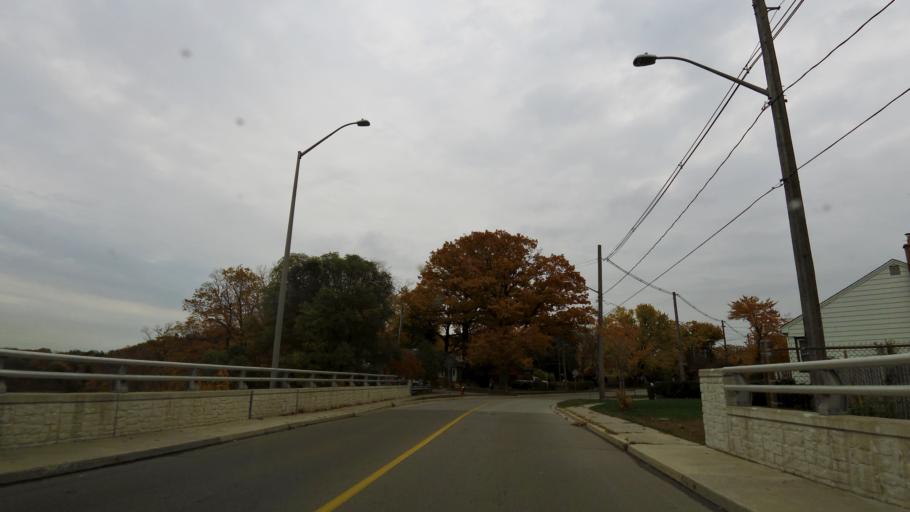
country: CA
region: Ontario
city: Oakville
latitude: 43.4496
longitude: -79.6856
